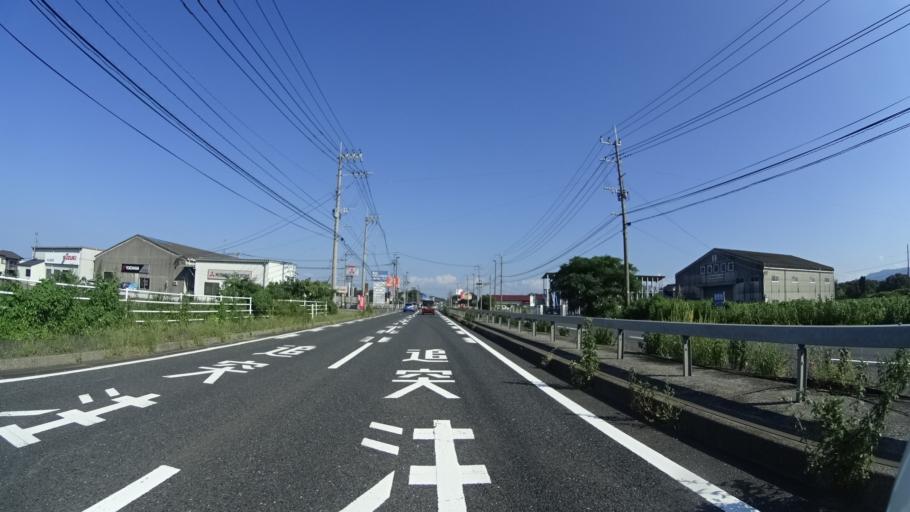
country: JP
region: Fukuoka
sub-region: Buzen-shi
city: Buzen
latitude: 33.5930
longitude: 131.1459
